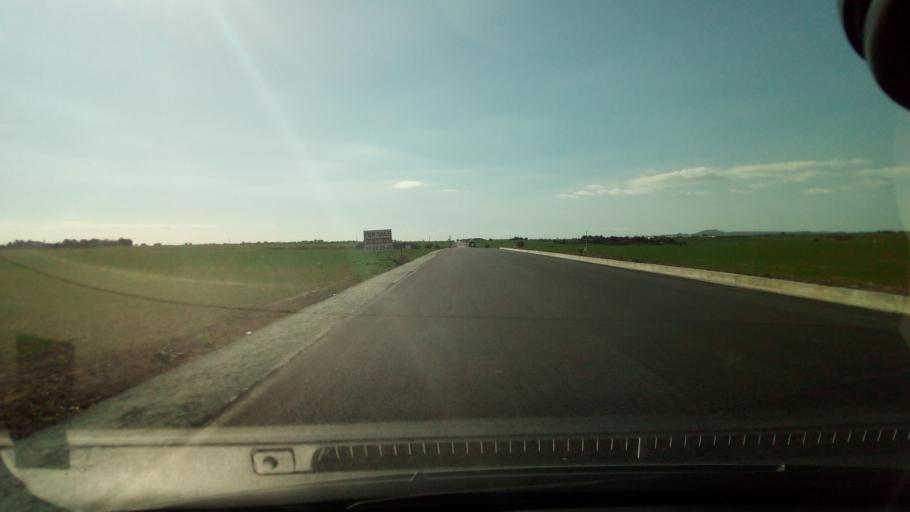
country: CY
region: Larnaka
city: Tersefanou
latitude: 34.8287
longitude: 33.5416
